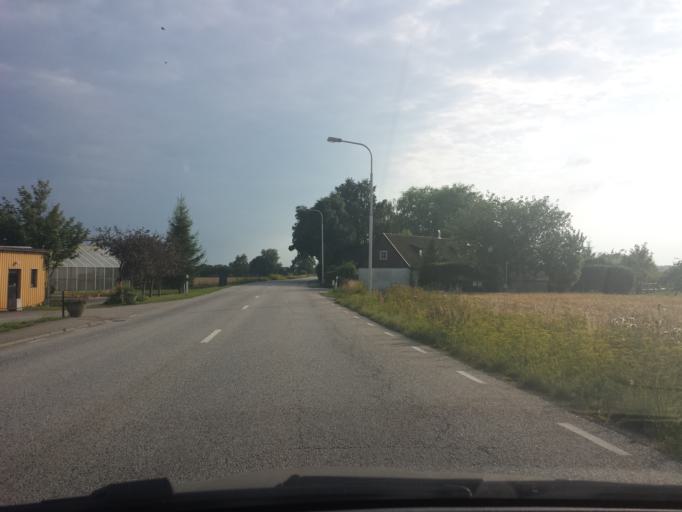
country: SE
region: Skane
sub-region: Ystads Kommun
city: Kopingebro
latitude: 55.4472
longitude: 14.0155
